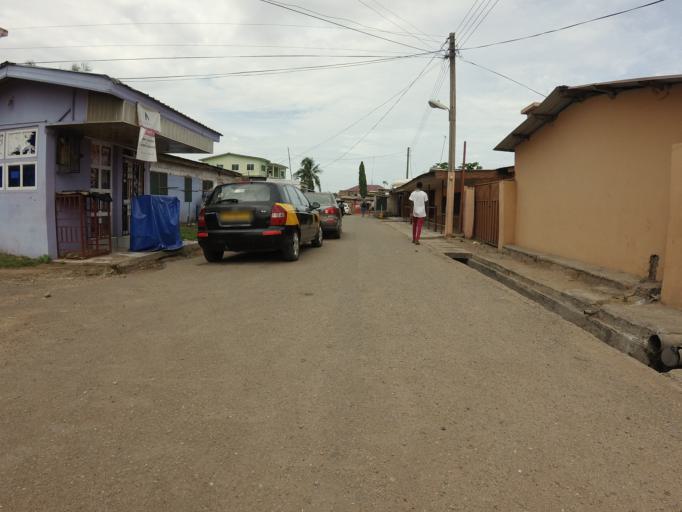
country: GH
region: Greater Accra
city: Accra
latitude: 5.5958
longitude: -0.2146
